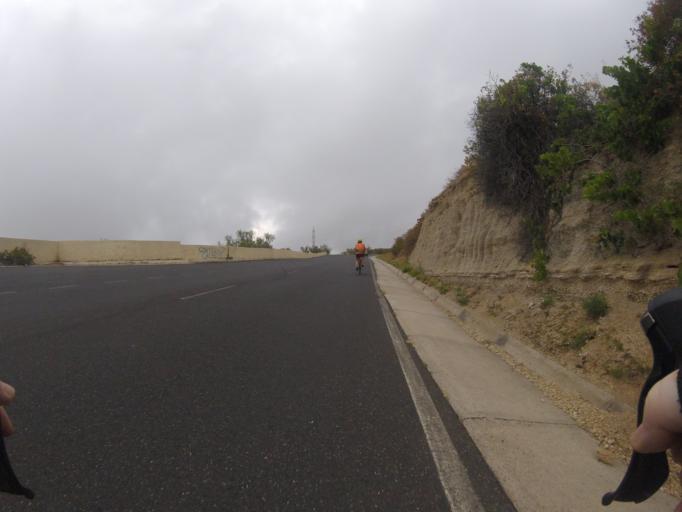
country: ES
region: Canary Islands
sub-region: Provincia de Santa Cruz de Tenerife
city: Guimar
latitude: 28.2941
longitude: -16.4029
